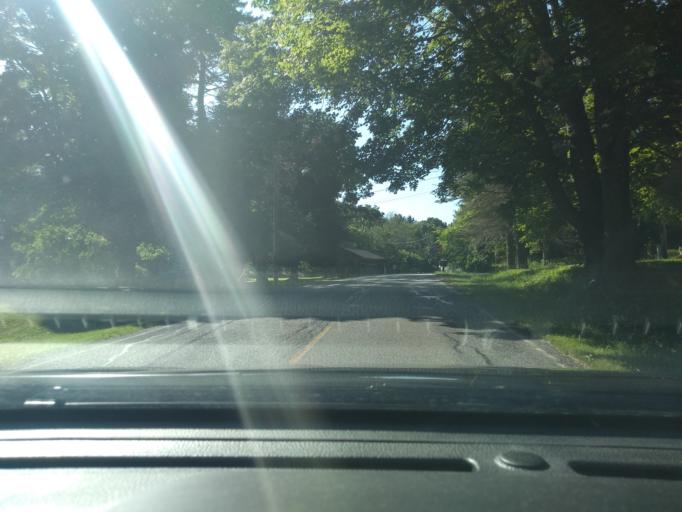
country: US
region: New York
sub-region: Erie County
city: Billington Heights
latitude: 42.7833
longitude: -78.6853
